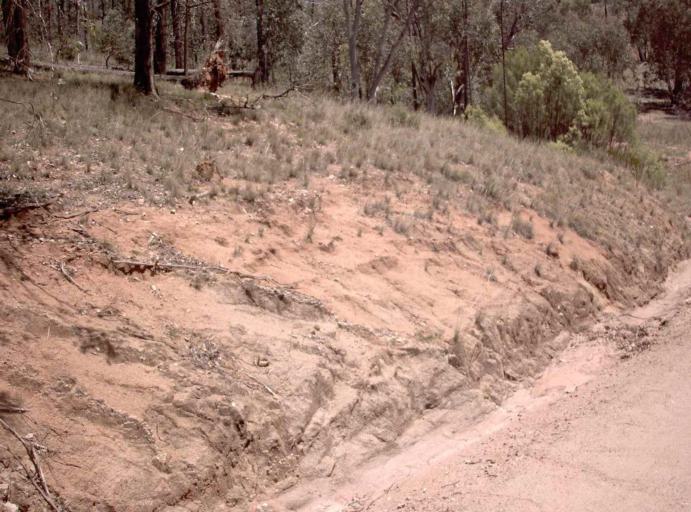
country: AU
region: New South Wales
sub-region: Snowy River
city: Jindabyne
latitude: -36.9253
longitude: 148.3898
